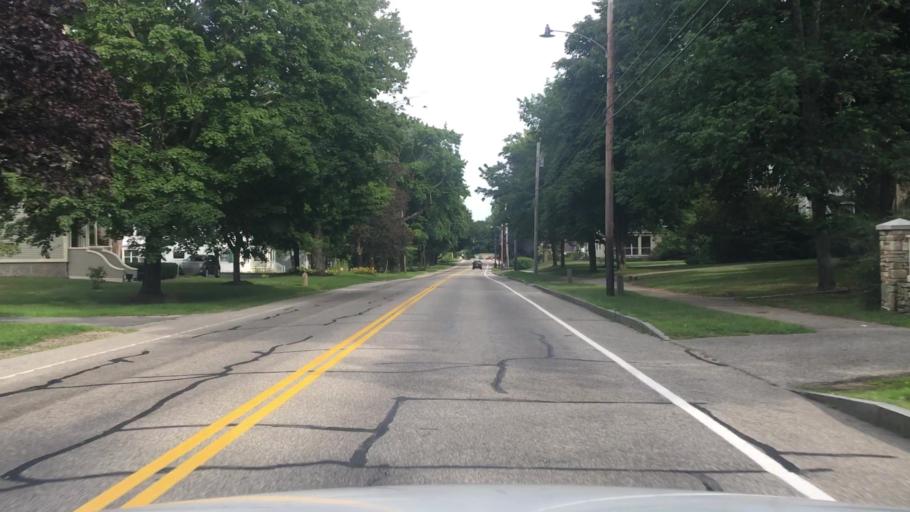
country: US
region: Maine
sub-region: York County
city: Kennebunk
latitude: 43.3851
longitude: -70.5309
